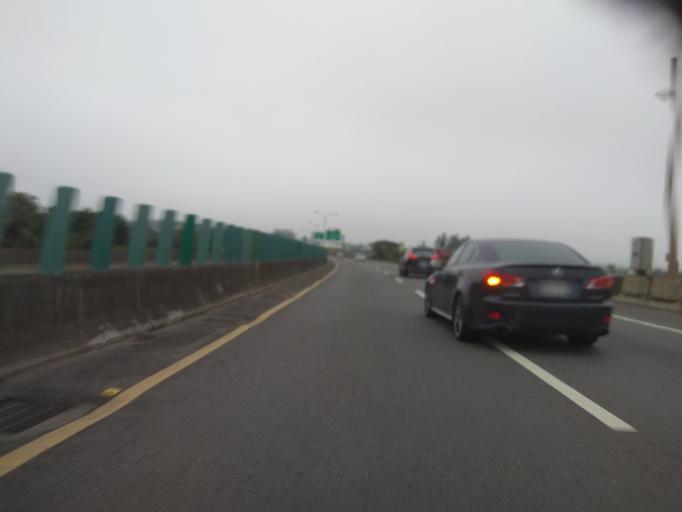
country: TW
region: Taiwan
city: Taoyuan City
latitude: 24.9614
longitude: 121.1360
